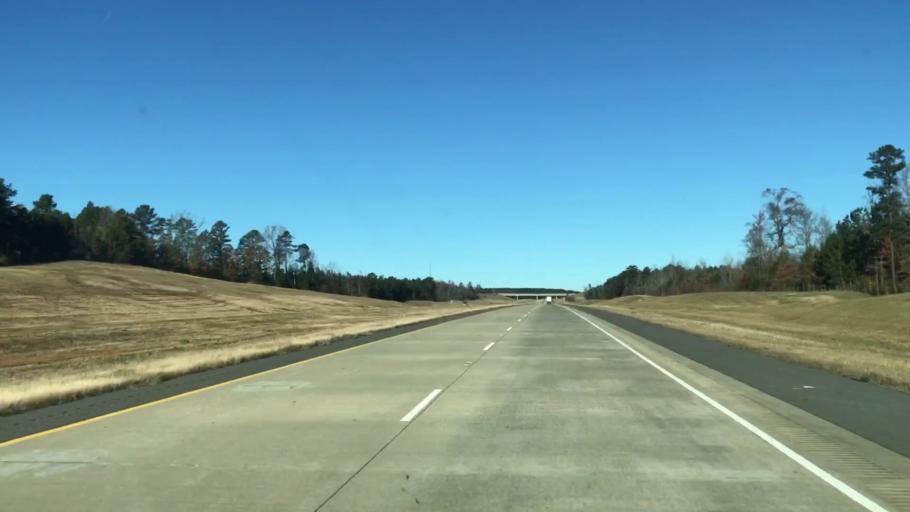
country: US
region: Louisiana
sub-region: Caddo Parish
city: Vivian
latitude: 32.9143
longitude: -93.8755
